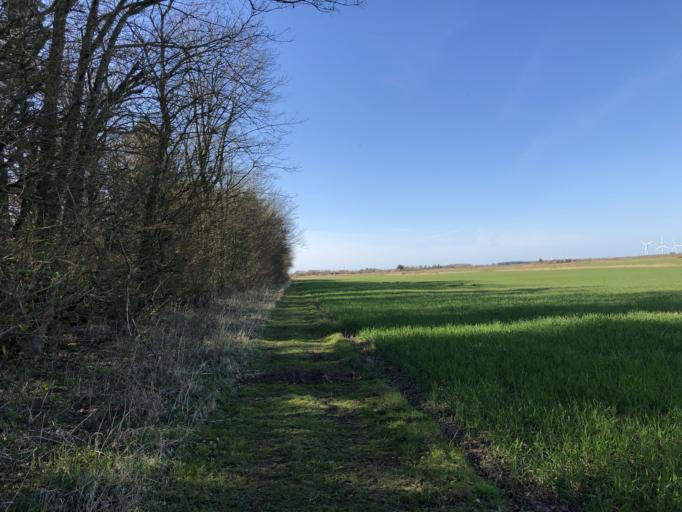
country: DK
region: Central Jutland
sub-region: Holstebro Kommune
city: Ulfborg
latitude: 56.3263
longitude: 8.3190
